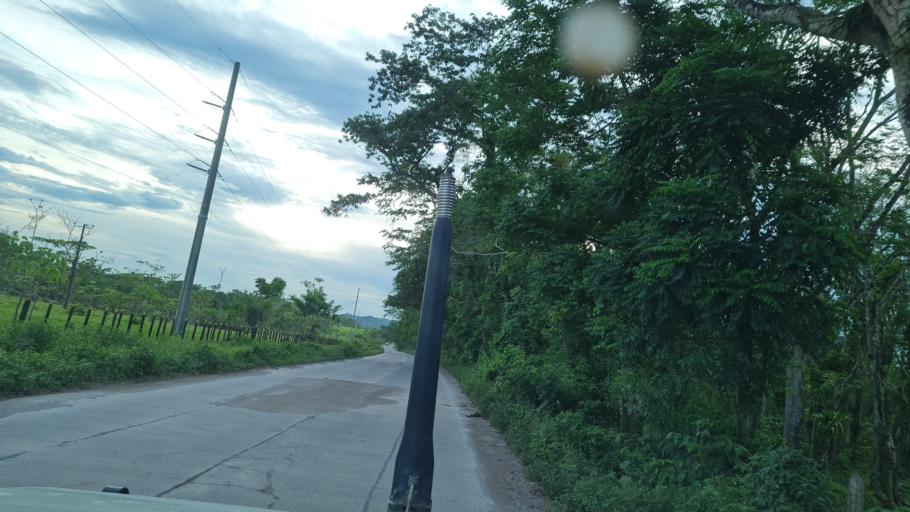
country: NI
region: Atlantico Norte (RAAN)
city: Siuna
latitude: 13.6844
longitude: -84.5961
